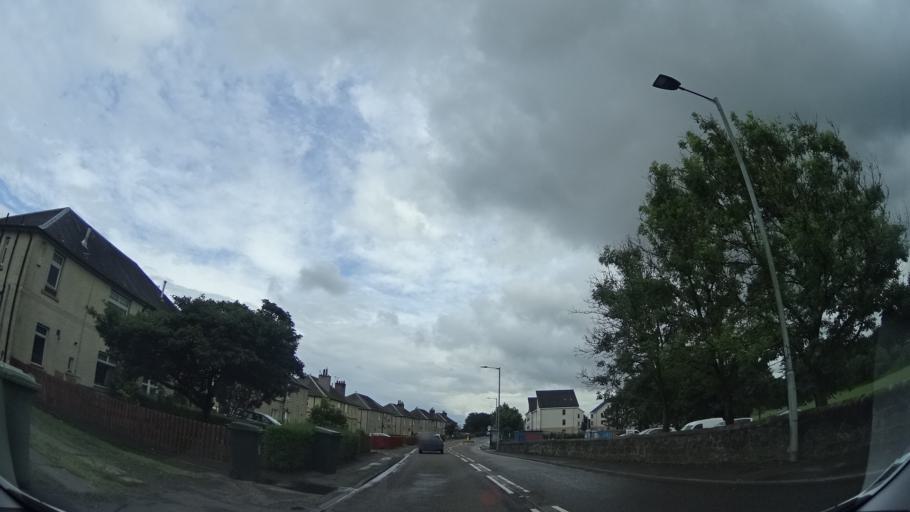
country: GB
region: Scotland
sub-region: Falkirk
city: Bonnybridge
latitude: 56.0039
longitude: -3.8761
